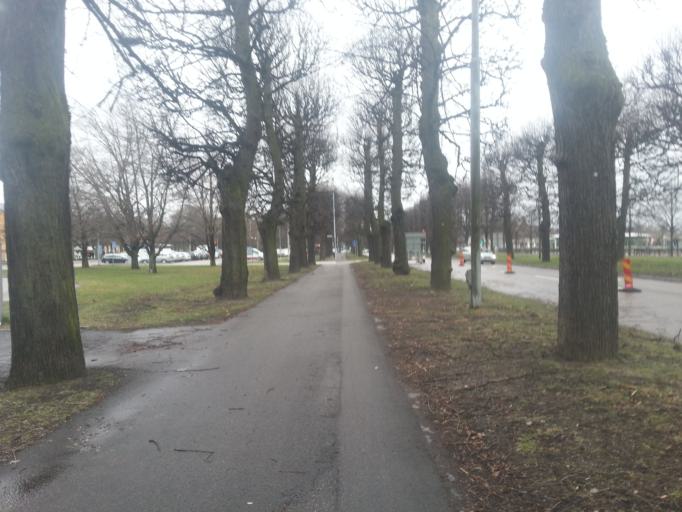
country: SE
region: OEstergoetland
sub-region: Norrkopings Kommun
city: Norrkoping
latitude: 58.5964
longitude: 16.1880
